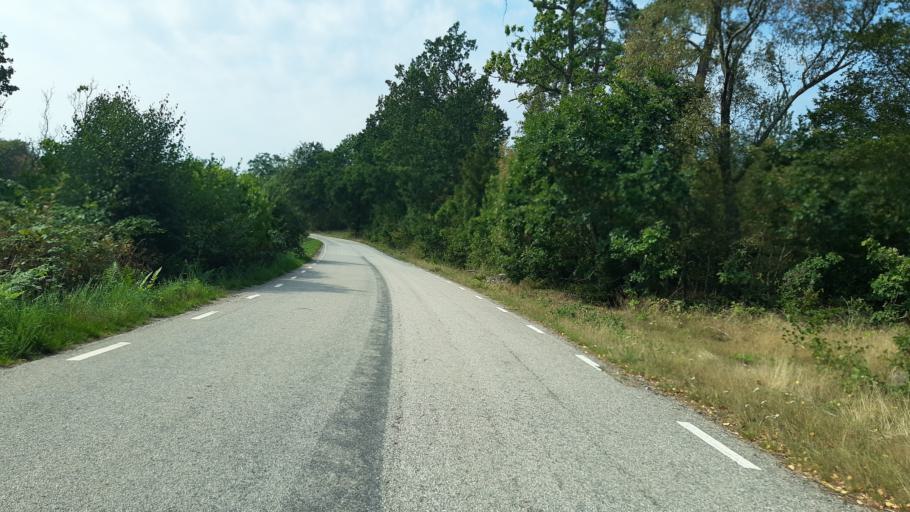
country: SE
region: Blekinge
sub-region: Karlskrona Kommun
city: Nattraby
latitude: 56.2176
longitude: 15.4446
